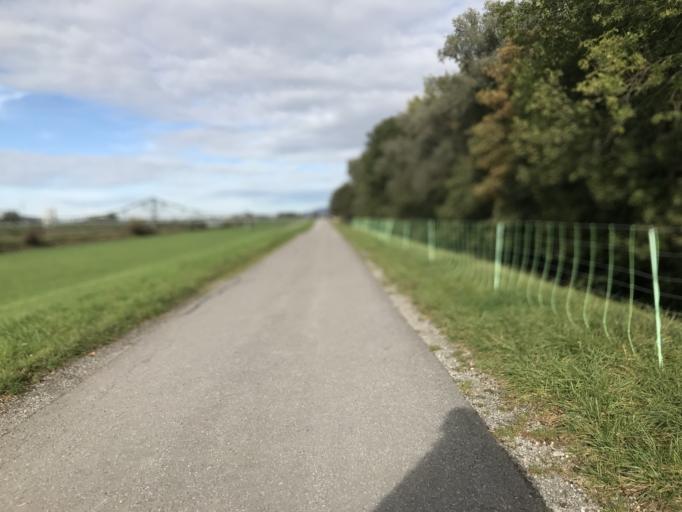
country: CH
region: Saint Gallen
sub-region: Wahlkreis Rheintal
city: Diepoldsau
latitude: 47.3800
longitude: 9.6413
